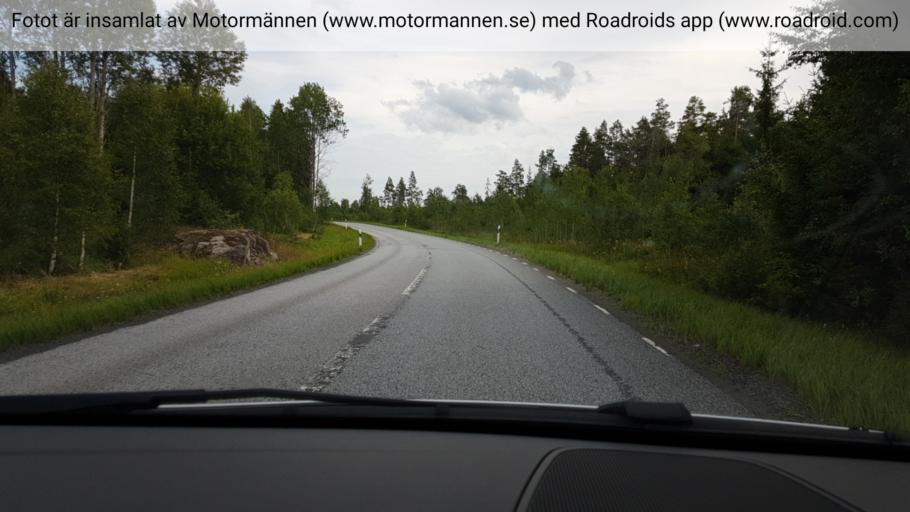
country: SE
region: Uppsala
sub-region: Osthammars Kommun
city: Anneberg
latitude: 60.1301
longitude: 18.4350
